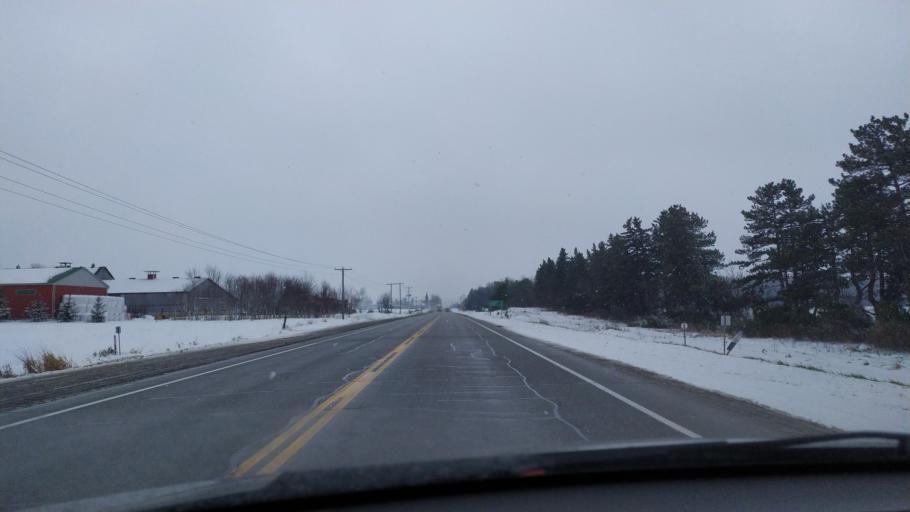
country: CA
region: Ontario
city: Waterloo
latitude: 43.6267
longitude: -80.7020
